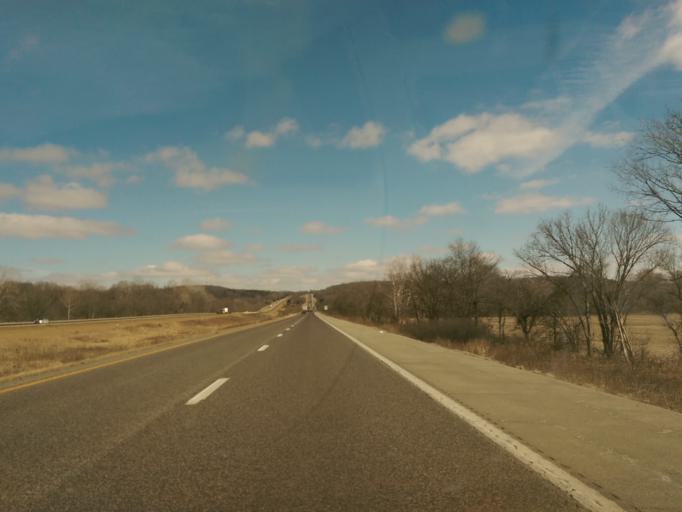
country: US
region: Missouri
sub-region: Montgomery County
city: Montgomery City
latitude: 38.8989
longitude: -91.5891
